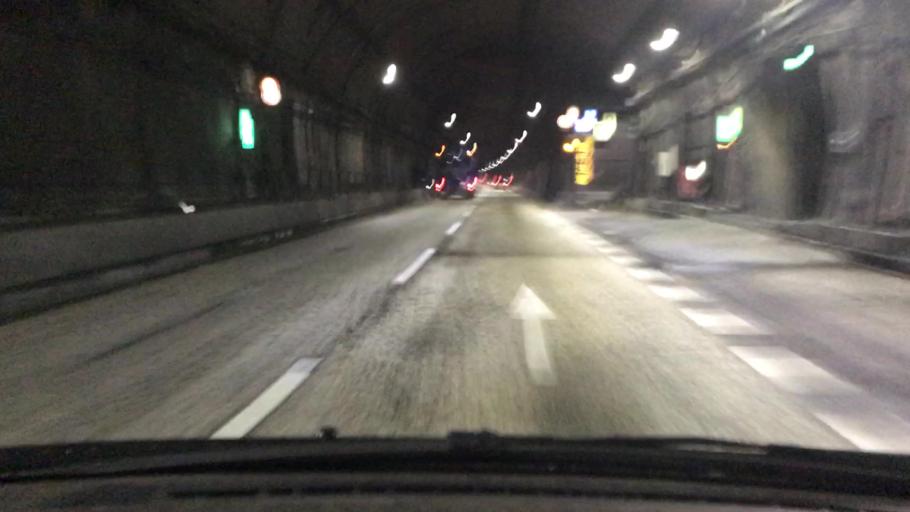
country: JP
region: Hyogo
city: Kobe
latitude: 34.7077
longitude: 135.1943
